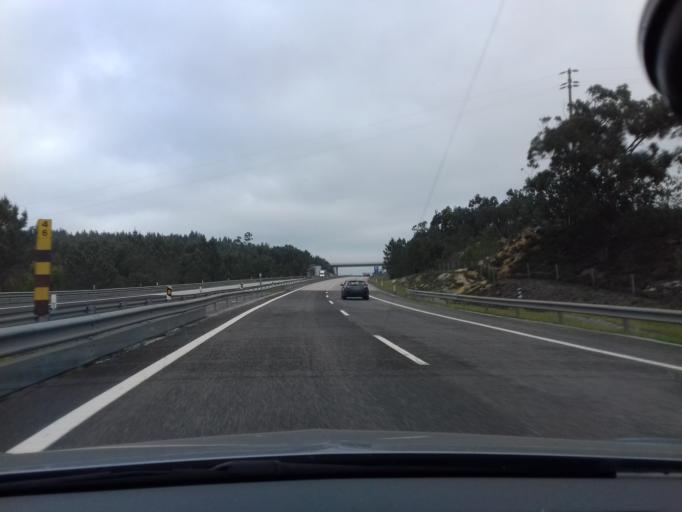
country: PT
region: Lisbon
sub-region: Torres Vedras
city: A dos Cunhados
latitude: 39.1408
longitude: -9.2478
